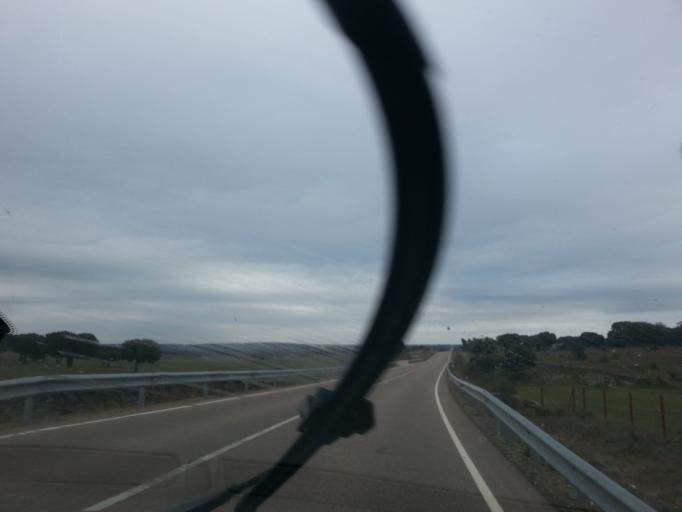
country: ES
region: Castille and Leon
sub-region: Provincia de Salamanca
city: Narros de Matalayegua
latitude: 40.7402
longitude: -5.9308
